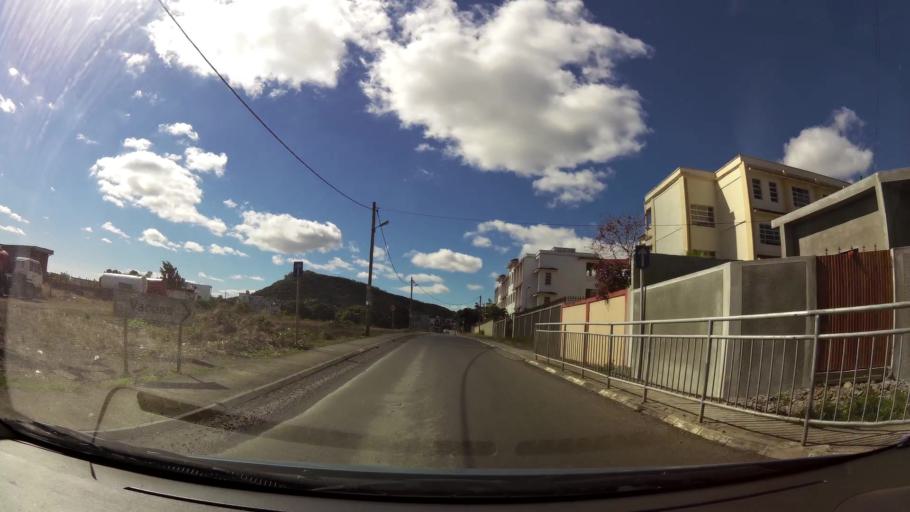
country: MU
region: Plaines Wilhems
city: Vacoas
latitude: -20.2856
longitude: 57.4782
